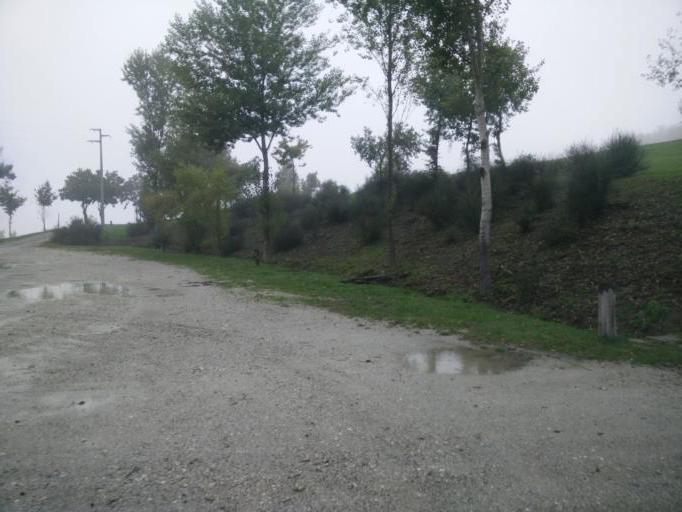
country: IT
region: Emilia-Romagna
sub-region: Provincia di Bologna
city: Marzabotto
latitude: 44.3112
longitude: 11.1968
